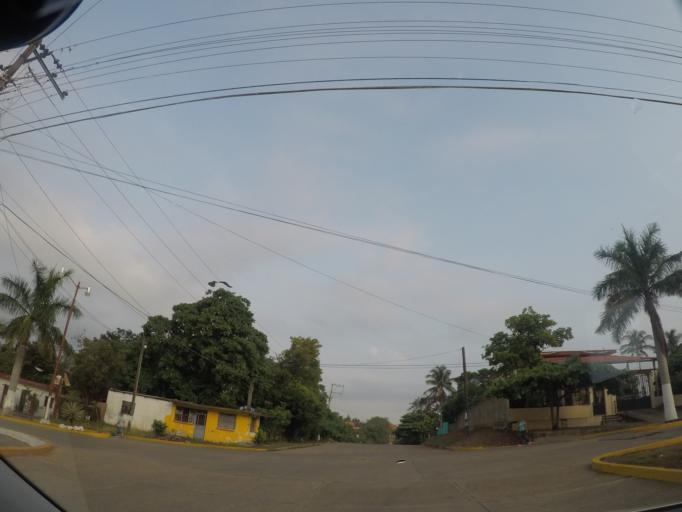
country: MX
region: Oaxaca
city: Matias Romero
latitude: 16.8719
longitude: -95.0431
